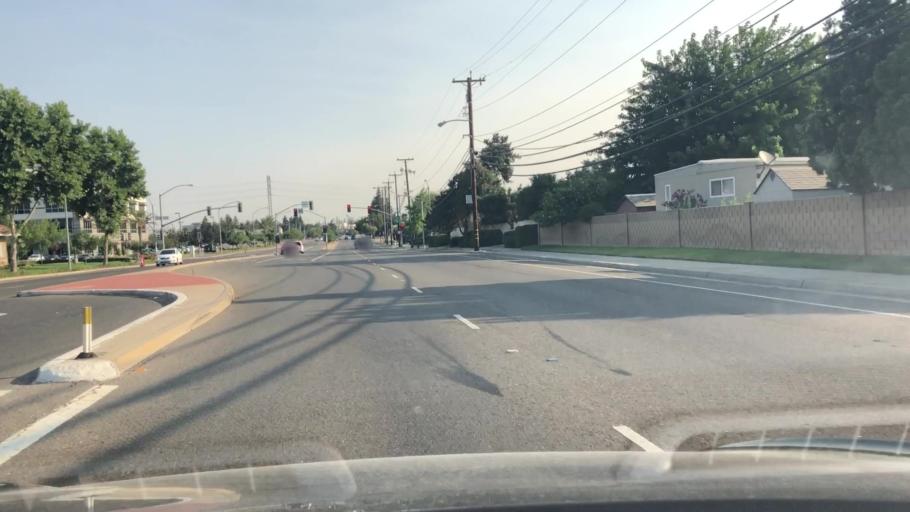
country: US
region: California
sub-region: Fresno County
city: Clovis
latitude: 36.8471
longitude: -119.7838
